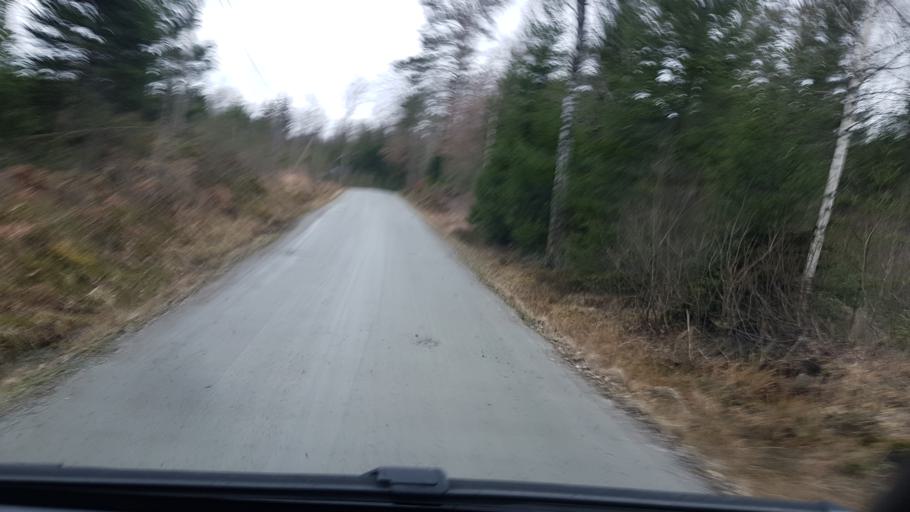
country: SE
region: Vaestra Goetaland
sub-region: Lerums Kommun
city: Stenkullen
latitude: 57.7993
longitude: 12.3843
